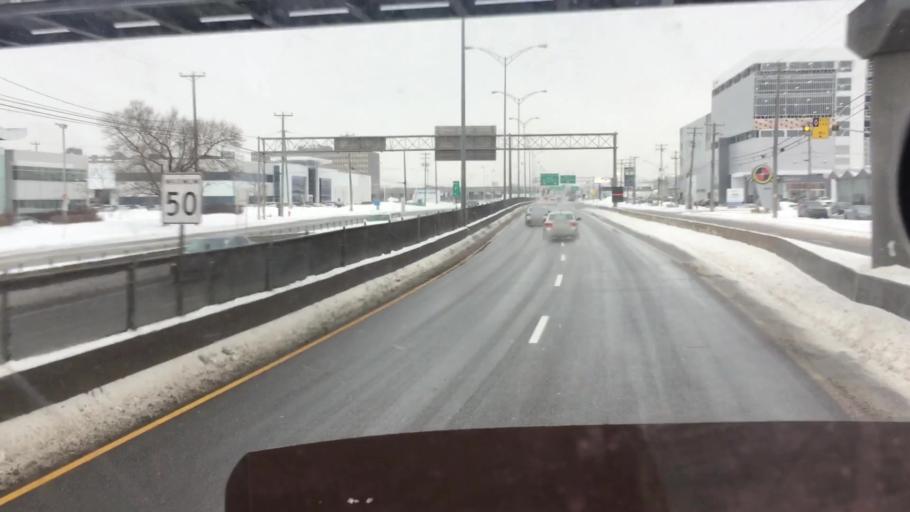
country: CA
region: Quebec
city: Saint-Laurent
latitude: 45.4914
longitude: -73.6813
